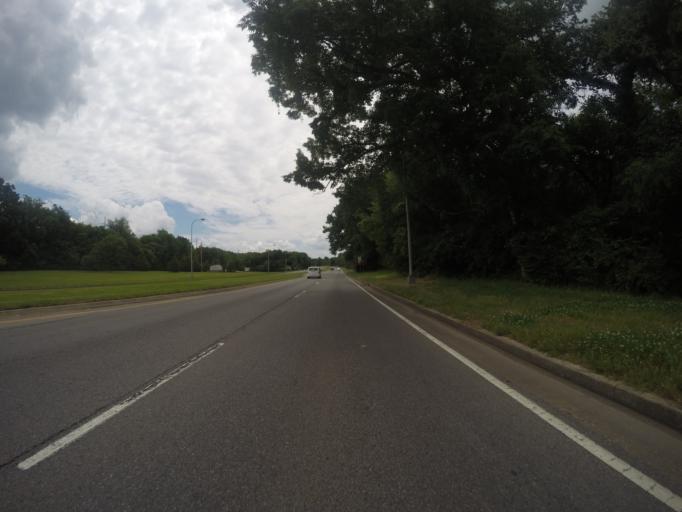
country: US
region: Tennessee
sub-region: Davidson County
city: Lakewood
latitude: 36.2116
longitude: -86.6229
